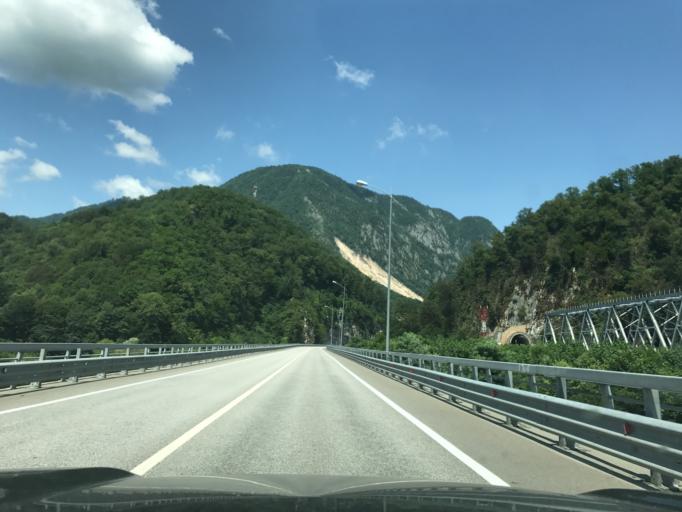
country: RU
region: Krasnodarskiy
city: Vysokoye
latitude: 43.5794
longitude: 40.0089
